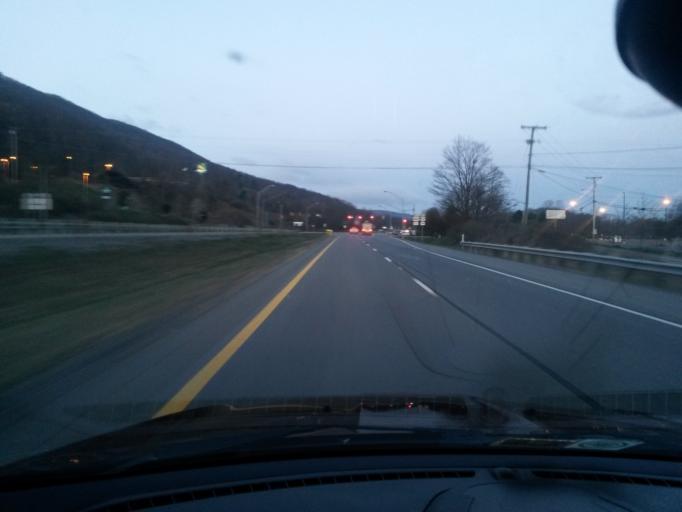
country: US
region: West Virginia
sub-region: Mercer County
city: Bluefield
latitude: 37.2628
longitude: -81.1859
